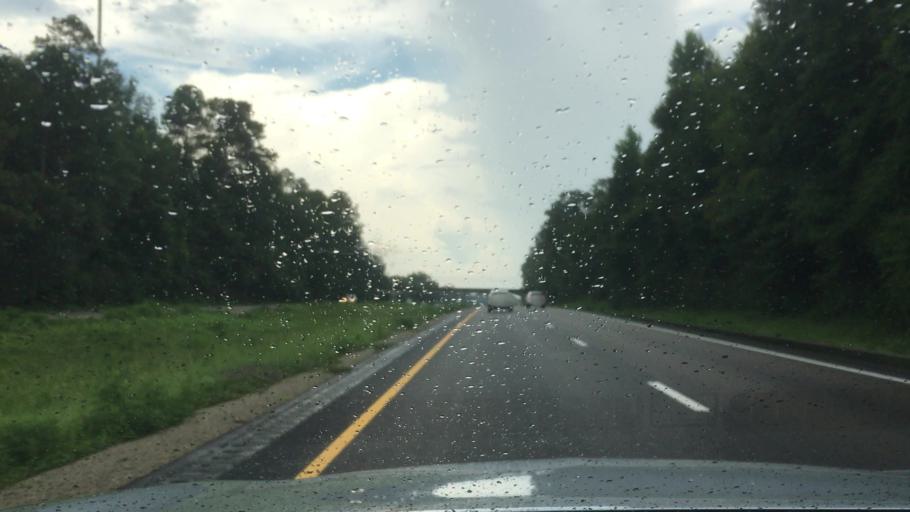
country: US
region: Mississippi
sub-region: Lamar County
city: Purvis
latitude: 31.1857
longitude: -89.3440
